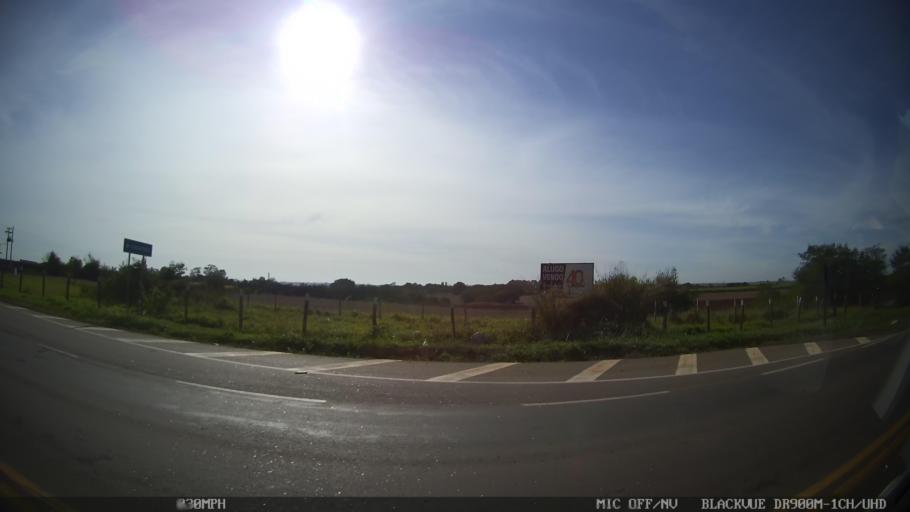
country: BR
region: Sao Paulo
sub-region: Piracicaba
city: Piracicaba
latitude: -22.7844
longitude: -47.6501
